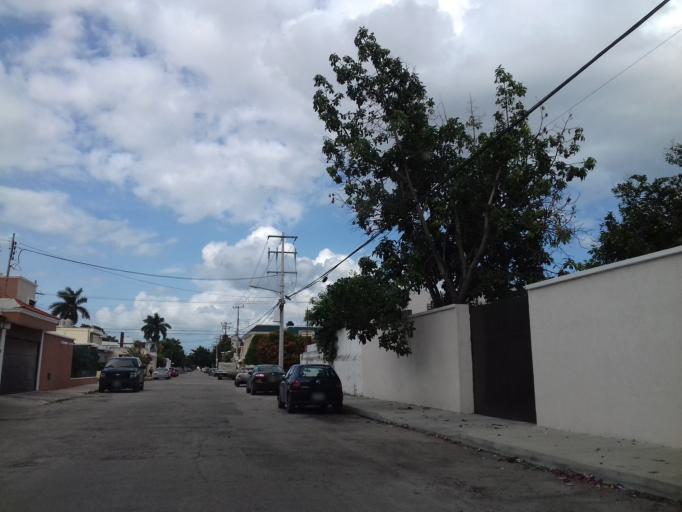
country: MX
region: Yucatan
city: Merida
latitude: 20.9996
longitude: -89.6140
